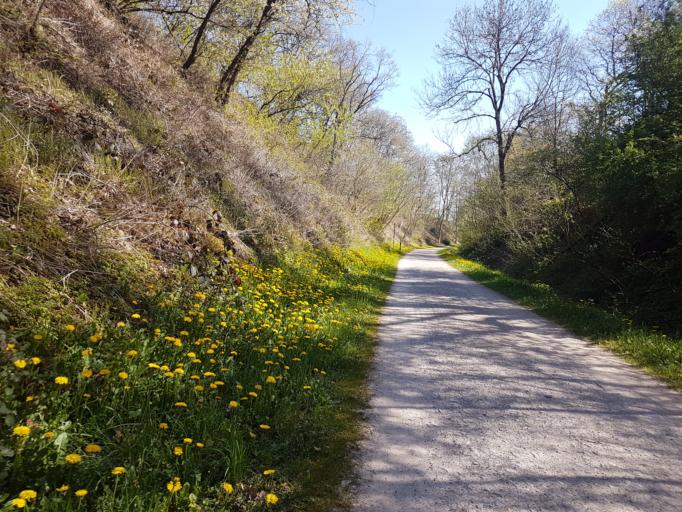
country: DE
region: North Rhine-Westphalia
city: Hattingen
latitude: 51.3764
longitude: 7.2128
